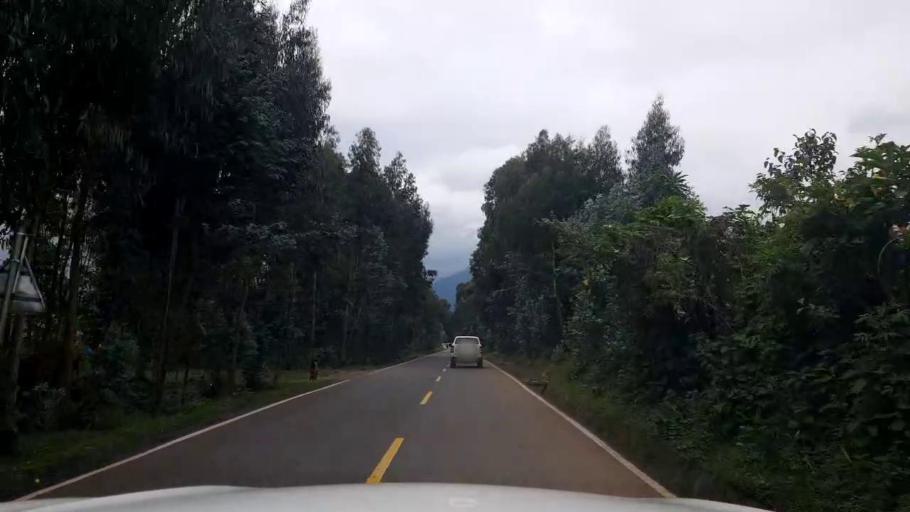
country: RW
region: Northern Province
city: Musanze
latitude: -1.4367
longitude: 29.5503
